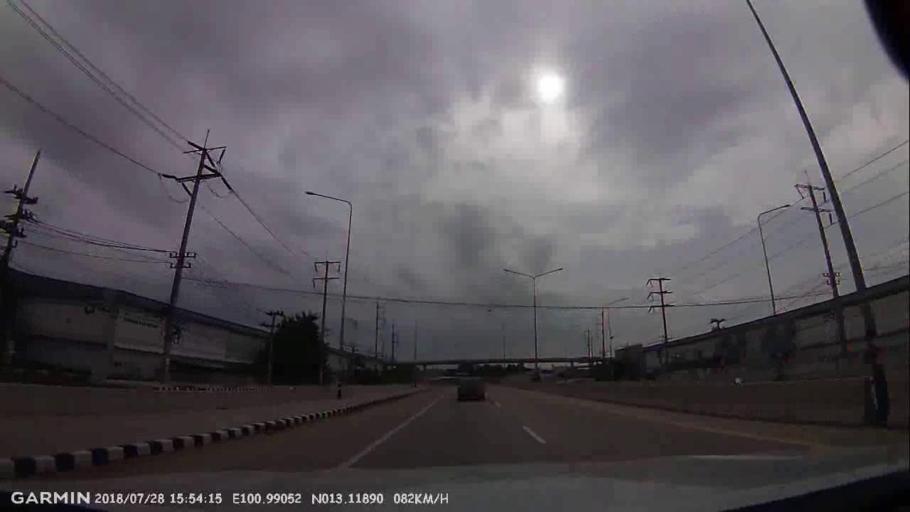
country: TH
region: Chon Buri
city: Ban Talat Bueng
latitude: 13.1189
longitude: 100.9903
